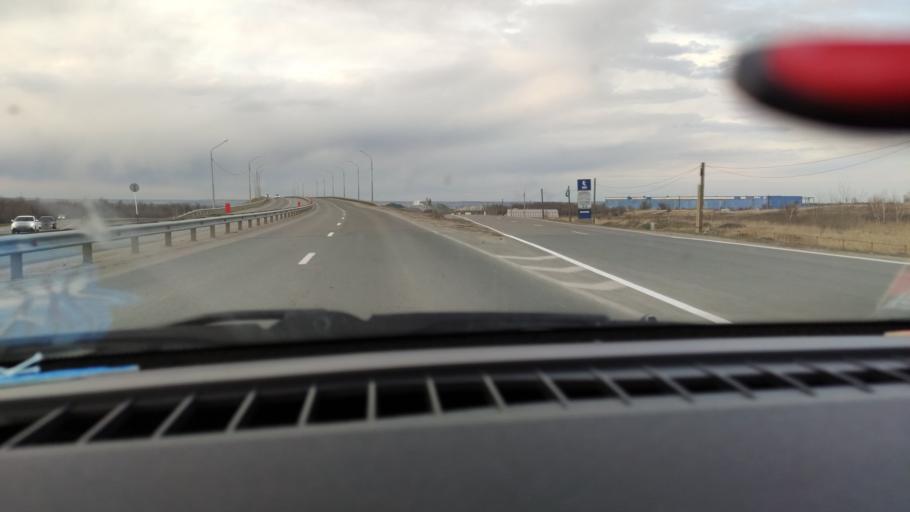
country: RU
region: Saratov
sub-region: Saratovskiy Rayon
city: Saratov
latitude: 51.6424
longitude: 45.9852
